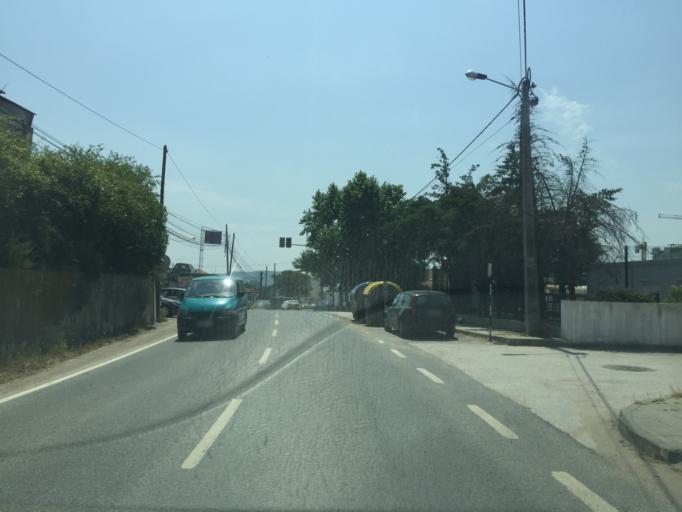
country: PT
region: Lisbon
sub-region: Loures
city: Loures
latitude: 38.8430
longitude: -9.1787
